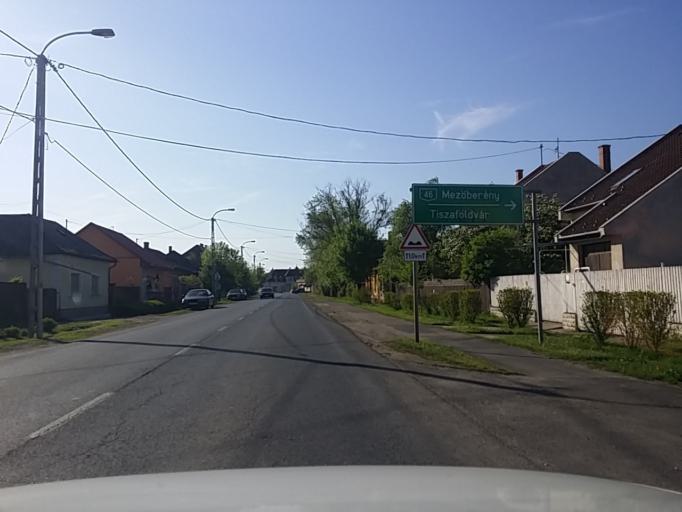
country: HU
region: Jasz-Nagykun-Szolnok
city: Mezotur
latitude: 47.0085
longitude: 20.6201
